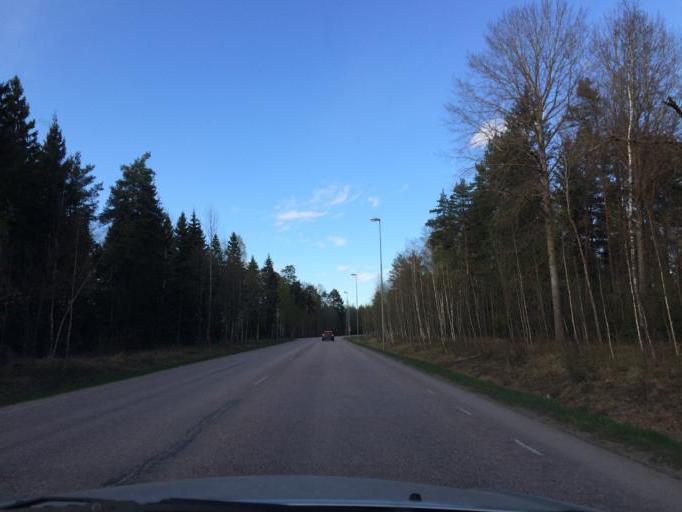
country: SE
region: Vaestmanland
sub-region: Vasteras
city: Vasteras
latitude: 59.6458
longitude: 16.5558
